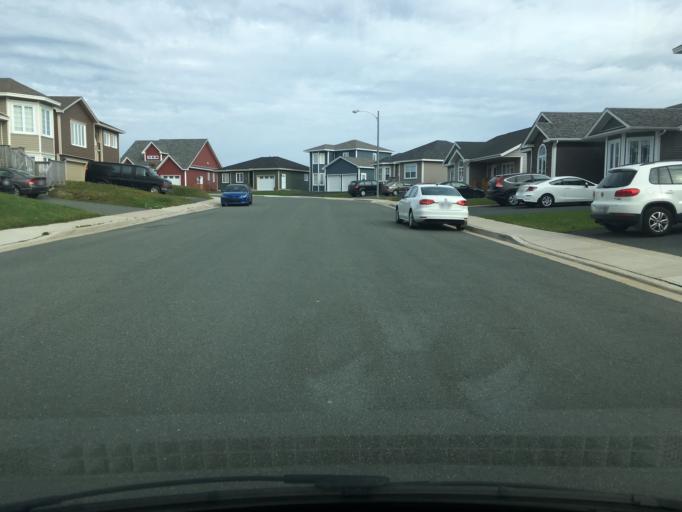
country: CA
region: Newfoundland and Labrador
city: Mount Pearl
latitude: 47.5510
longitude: -52.7865
